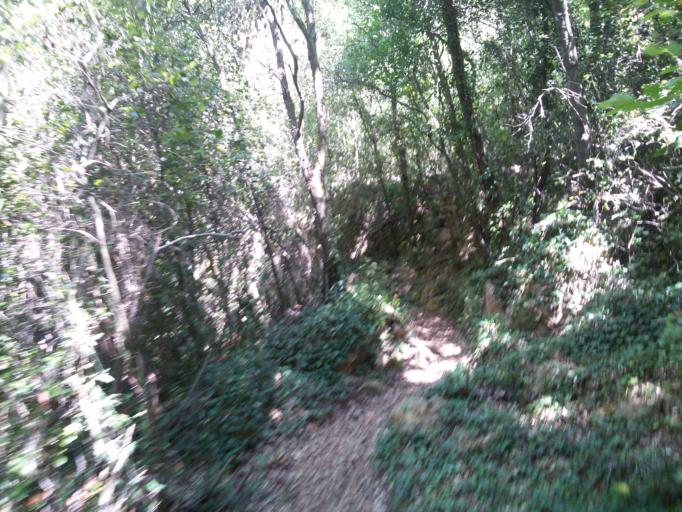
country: IT
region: Liguria
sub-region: Provincia di Savona
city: Borgio
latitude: 44.1712
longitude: 8.3178
